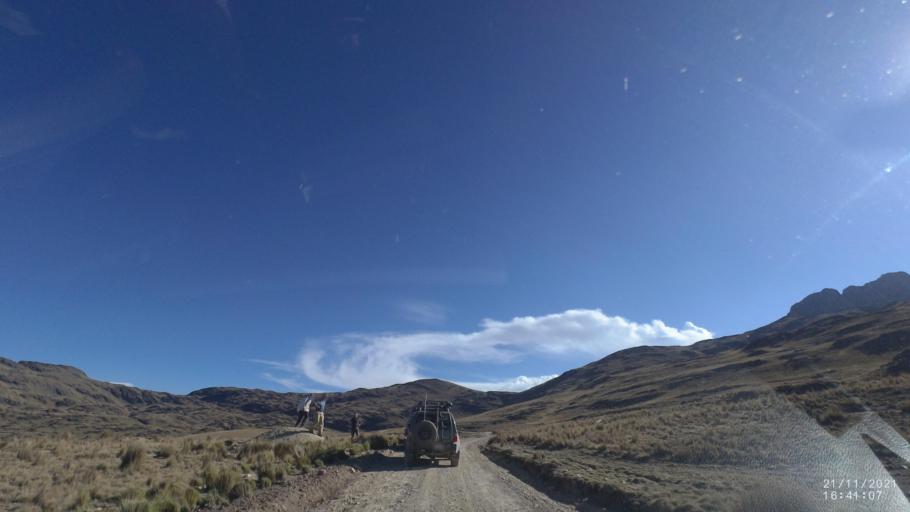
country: BO
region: Cochabamba
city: Cochabamba
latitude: -17.0649
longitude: -66.2561
